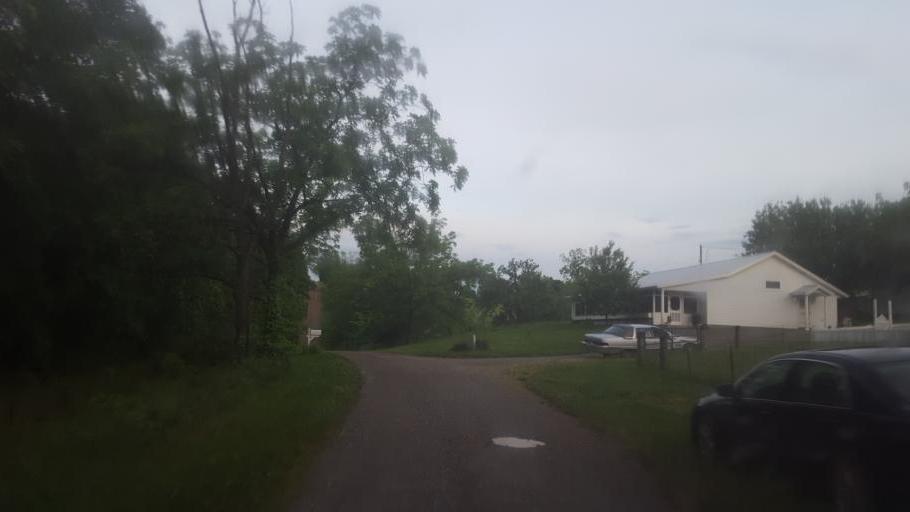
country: US
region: Missouri
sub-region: Moniteau County
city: California
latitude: 38.7245
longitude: -92.6246
